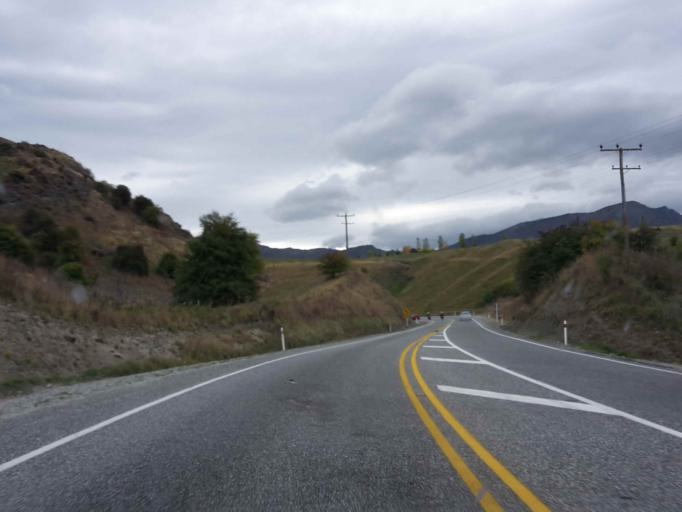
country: NZ
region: Otago
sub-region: Queenstown-Lakes District
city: Arrowtown
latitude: -44.9813
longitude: 168.8356
